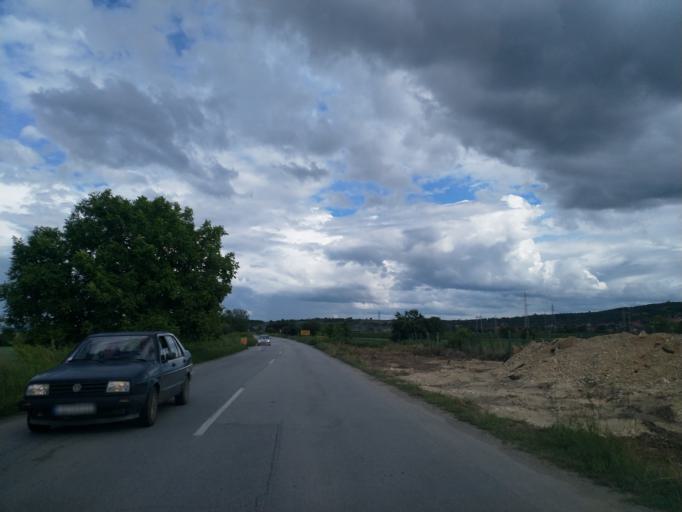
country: RS
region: Central Serbia
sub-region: Pomoravski Okrug
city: Jagodina
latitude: 43.9595
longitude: 21.2857
